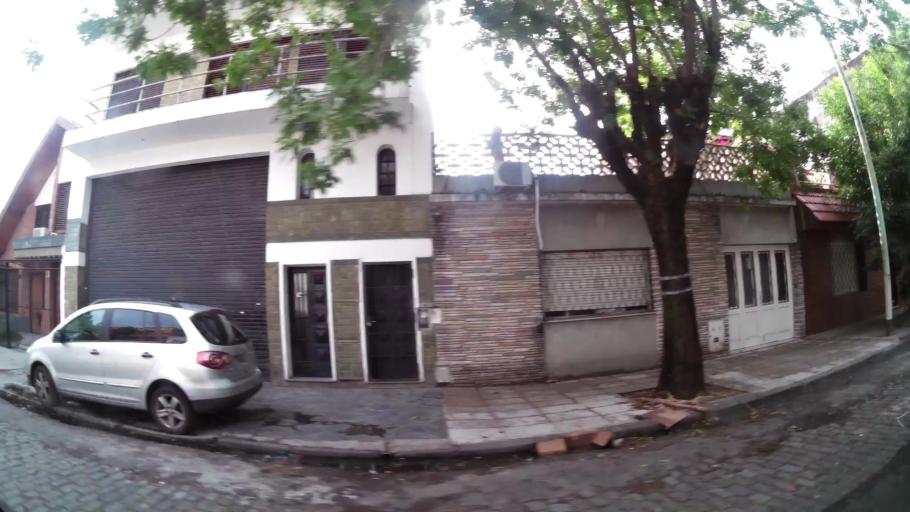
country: AR
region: Buenos Aires F.D.
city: Buenos Aires
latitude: -34.6417
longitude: -58.4145
